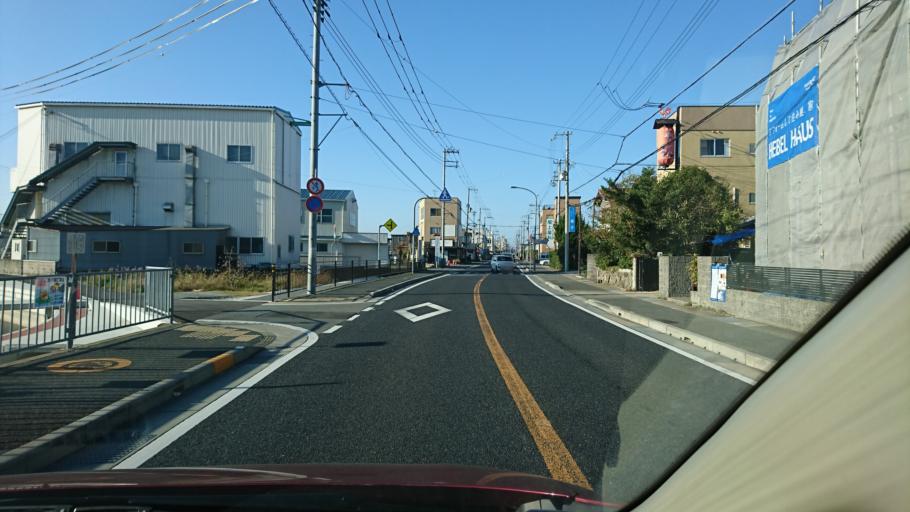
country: JP
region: Hyogo
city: Kakogawacho-honmachi
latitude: 34.7799
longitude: 134.8579
